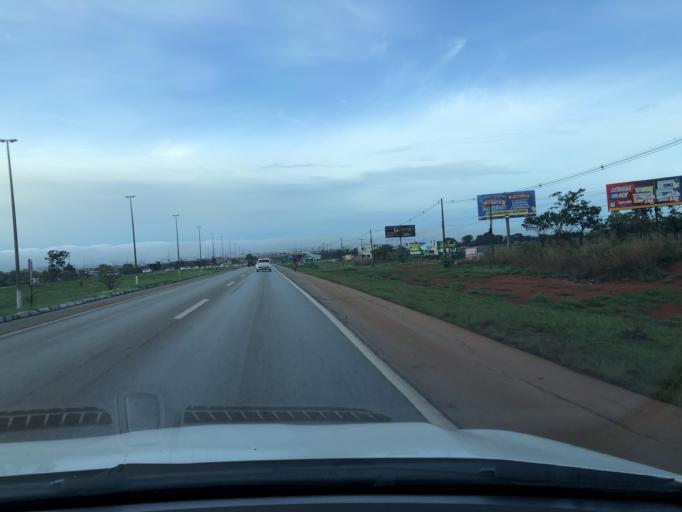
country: BR
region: Goias
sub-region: Luziania
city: Luziania
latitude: -16.0435
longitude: -47.9805
